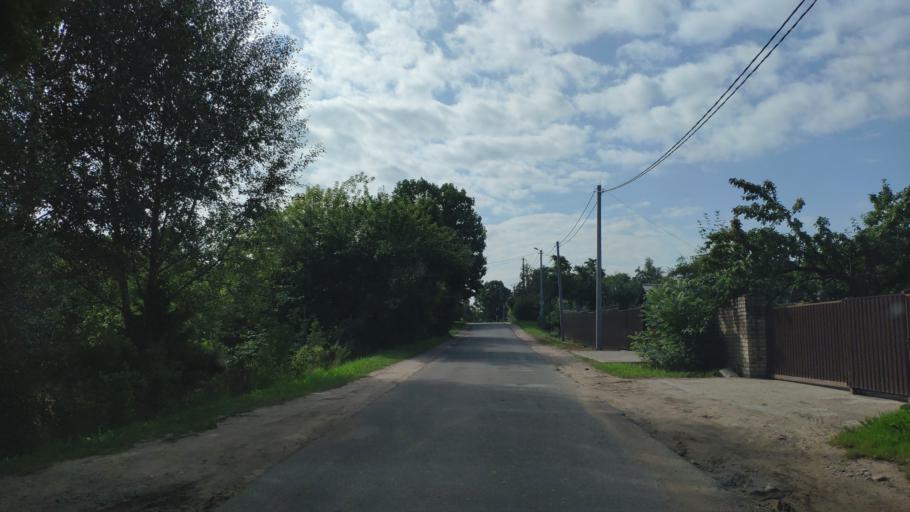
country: BY
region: Minsk
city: Zaslawye
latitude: 53.9981
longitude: 27.2807
